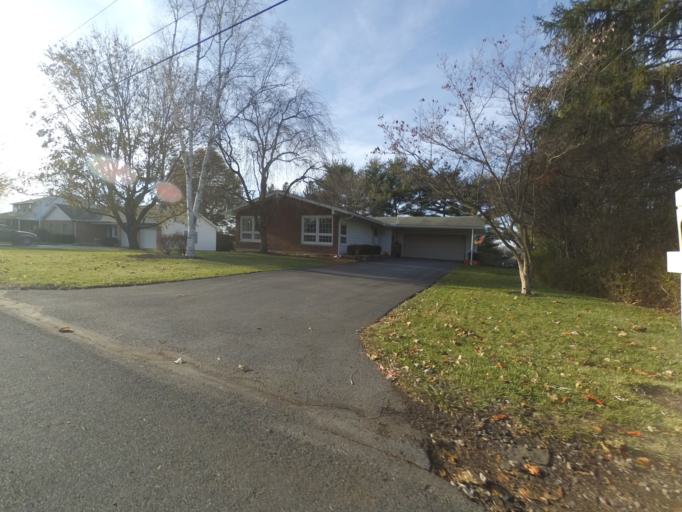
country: US
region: Pennsylvania
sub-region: Centre County
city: Lemont
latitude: 40.8027
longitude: -77.8234
